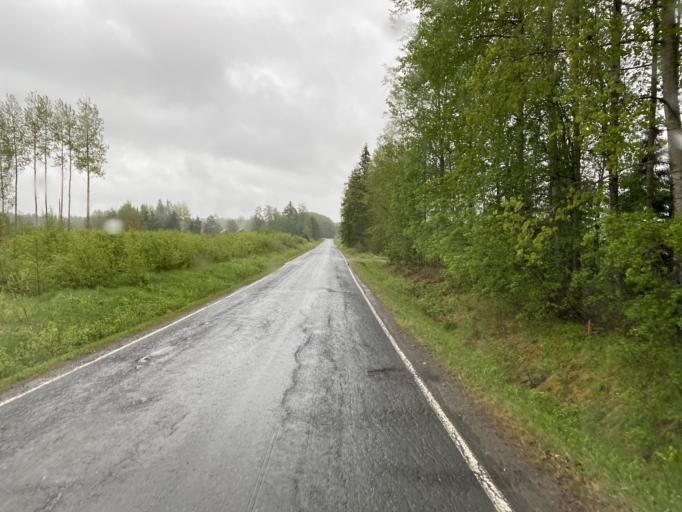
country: FI
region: Pirkanmaa
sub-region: Etelae-Pirkanmaa
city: Urjala
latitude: 60.9734
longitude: 23.5381
